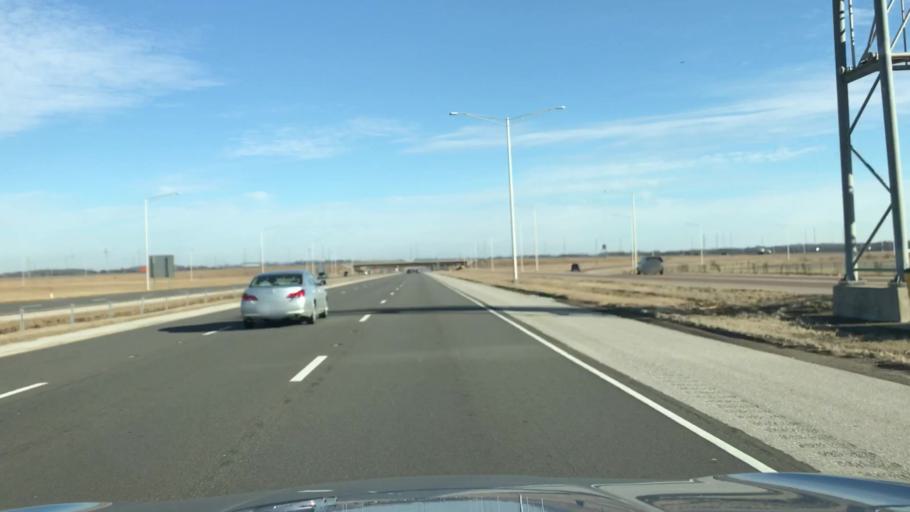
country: US
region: Illinois
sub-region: Madison County
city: Mitchell
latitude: 38.7573
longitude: -90.0504
